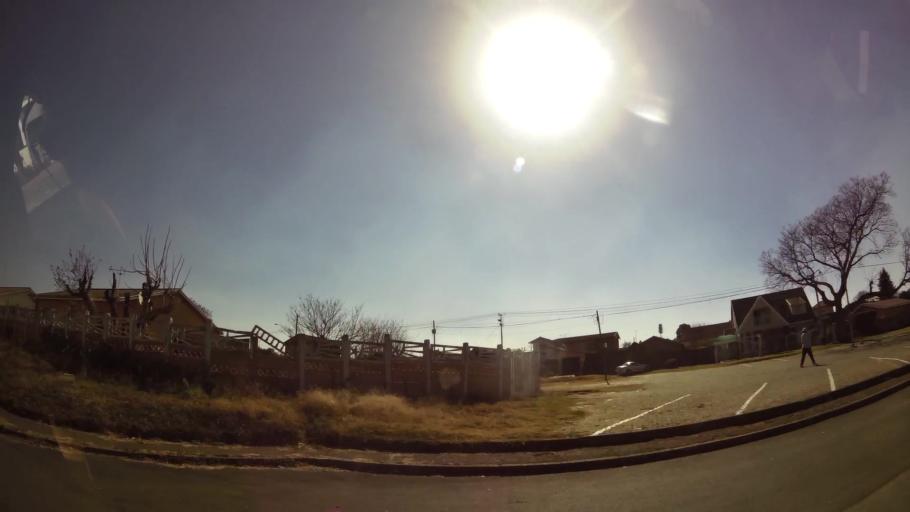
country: ZA
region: Gauteng
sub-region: City of Johannesburg Metropolitan Municipality
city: Johannesburg
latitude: -26.1904
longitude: 27.9564
